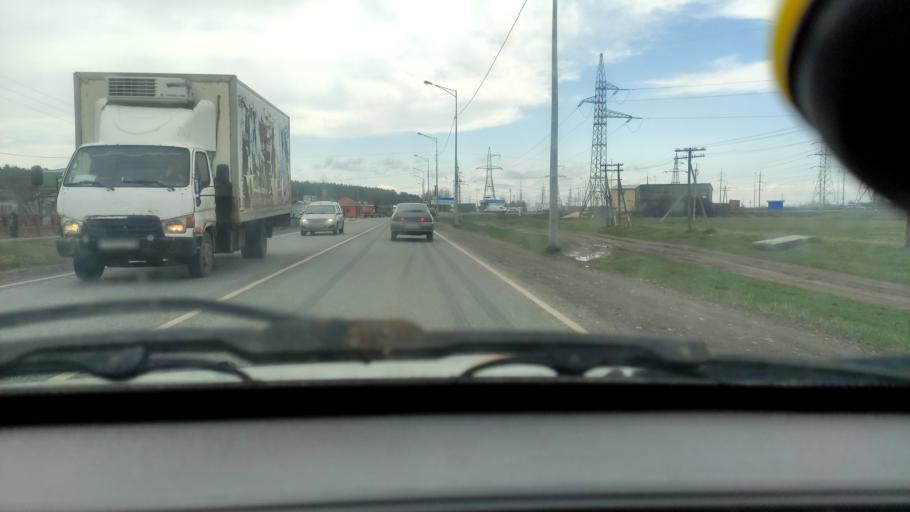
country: RU
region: Samara
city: Zhigulevsk
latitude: 53.5440
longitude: 49.5169
